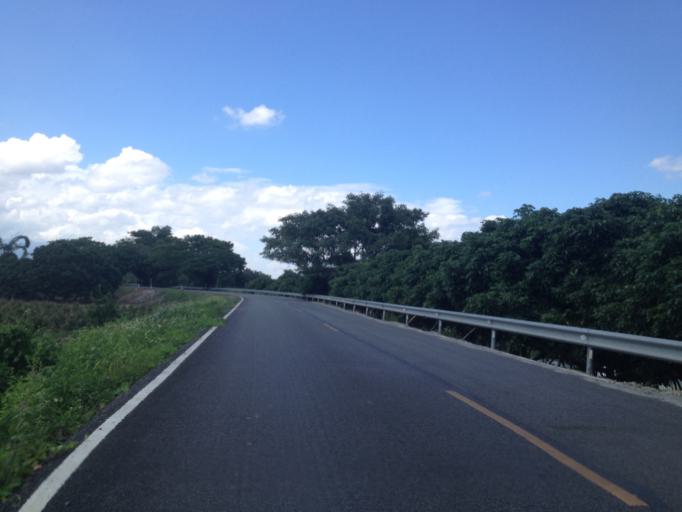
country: TH
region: Chiang Mai
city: Hang Dong
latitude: 18.6399
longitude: 98.9540
